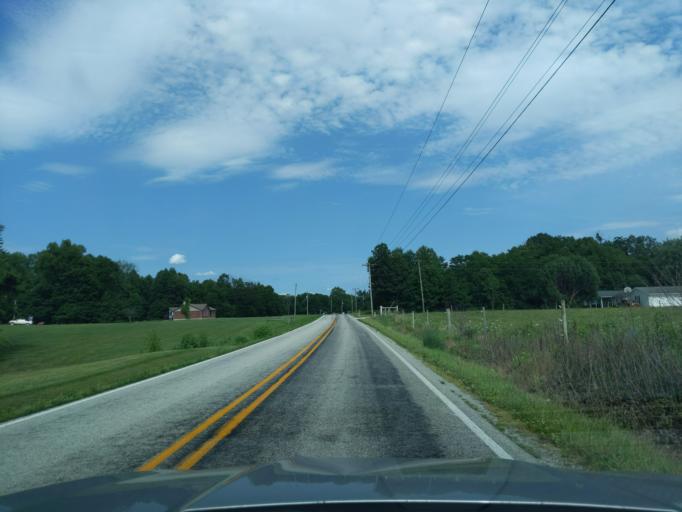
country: US
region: Indiana
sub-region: Ripley County
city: Osgood
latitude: 39.1953
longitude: -85.2696
